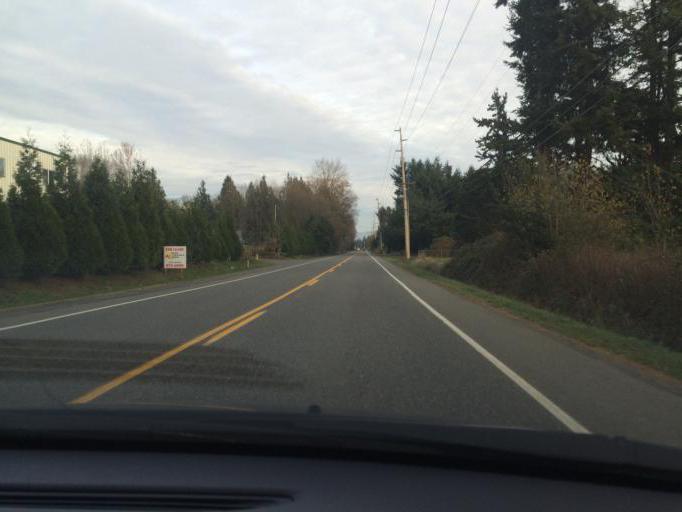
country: US
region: Washington
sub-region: Whatcom County
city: Ferndale
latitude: 48.8919
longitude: -122.5913
